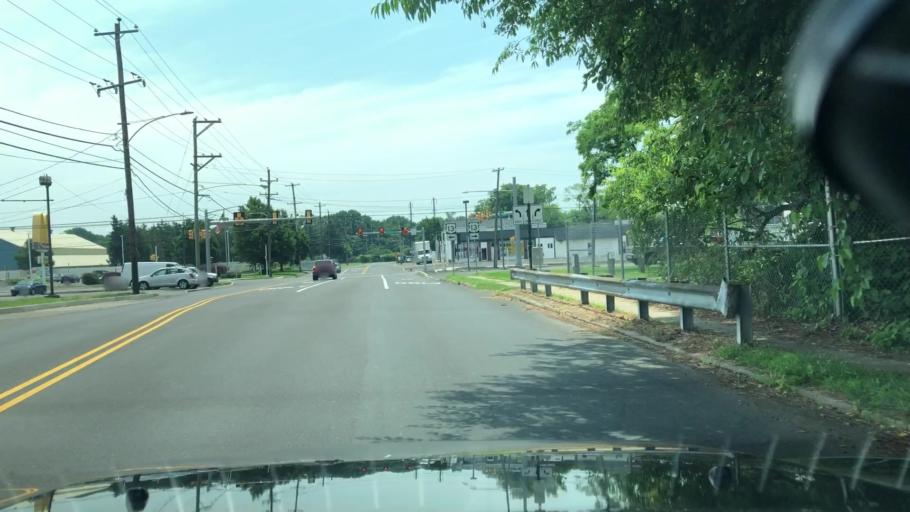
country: US
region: Pennsylvania
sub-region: Bucks County
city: Tullytown
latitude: 40.1335
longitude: -74.8307
